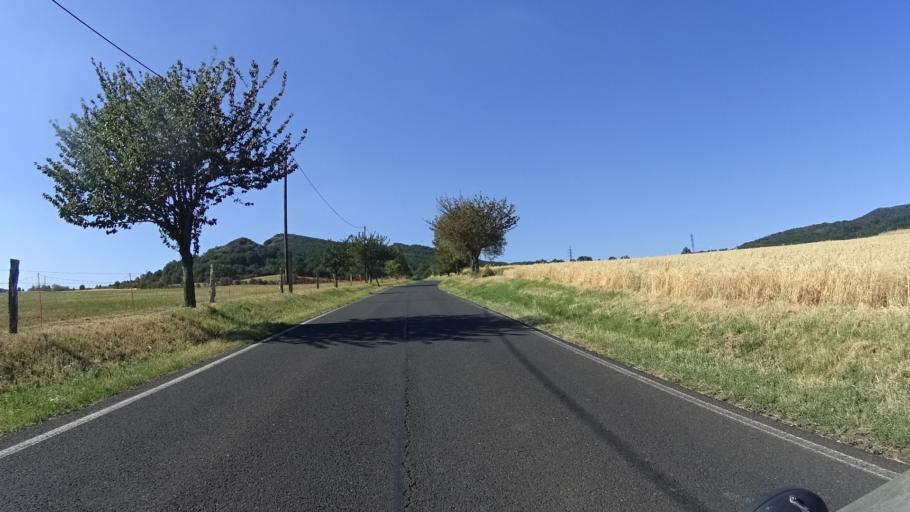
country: CZ
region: Ustecky
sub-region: Okres Litomerice
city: Litomerice
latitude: 50.5582
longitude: 14.1225
